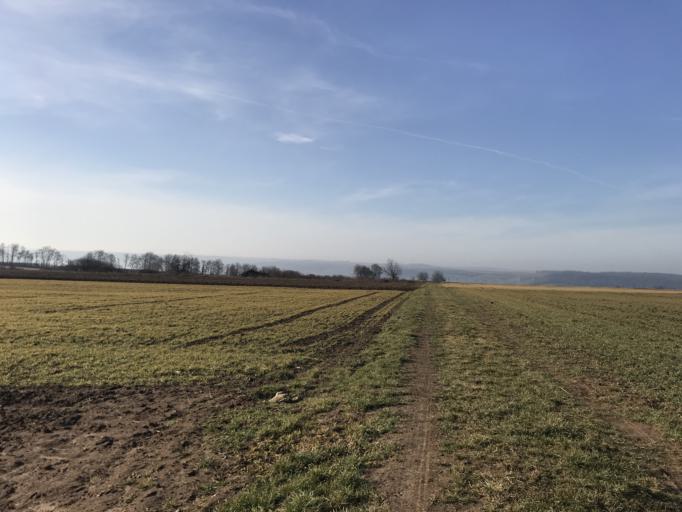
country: DE
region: Rheinland-Pfalz
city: Schwabenheim
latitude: 49.9457
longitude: 8.1024
